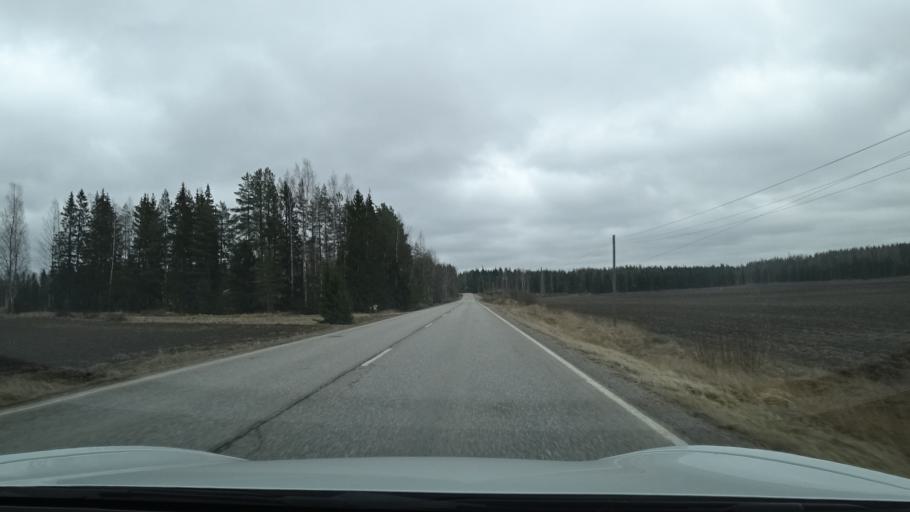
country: FI
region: Uusimaa
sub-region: Porvoo
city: Myrskylae
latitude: 60.6620
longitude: 25.7153
